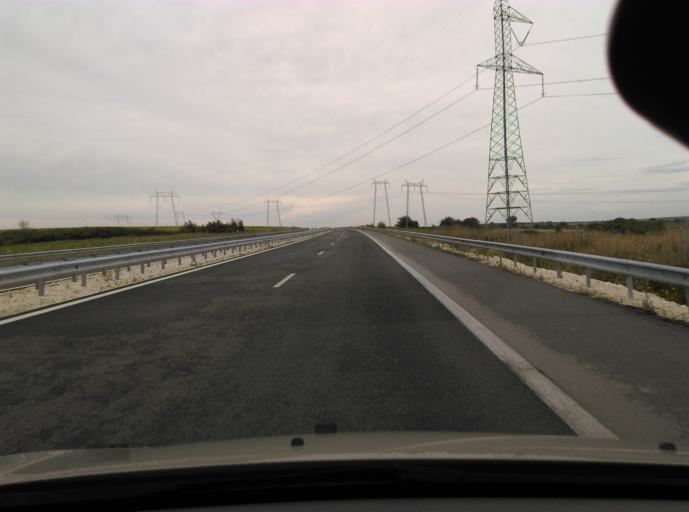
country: BG
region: Stara Zagora
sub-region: Obshtina Chirpan
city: Chirpan
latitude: 42.1277
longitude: 25.3661
